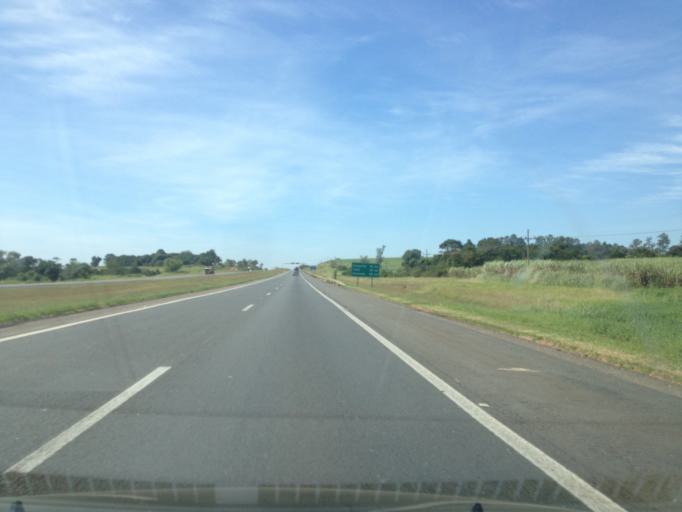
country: BR
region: Sao Paulo
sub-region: Tatui
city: Tatui
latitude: -23.2555
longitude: -47.9163
